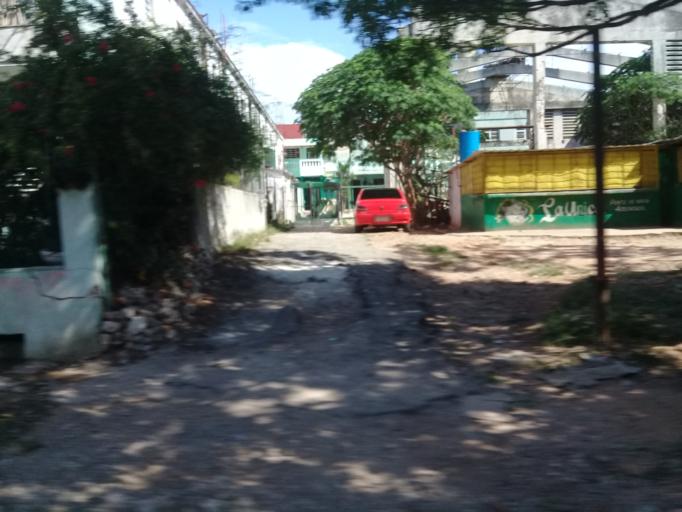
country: CU
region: La Habana
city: Havana
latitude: 23.1206
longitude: -82.4061
